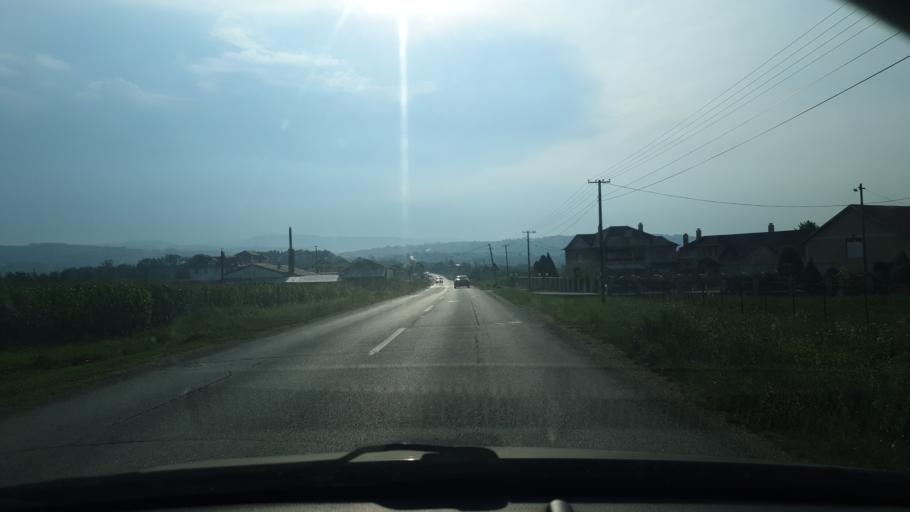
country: RS
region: Central Serbia
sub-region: Sumadijski Okrug
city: Topola
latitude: 44.1370
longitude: 20.7833
